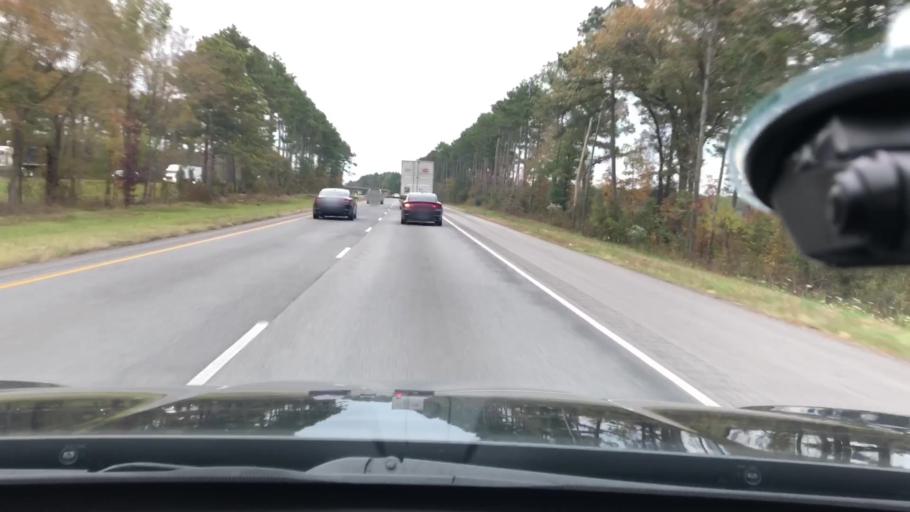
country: US
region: Arkansas
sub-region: Hempstead County
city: Hope
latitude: 33.6282
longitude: -93.7354
